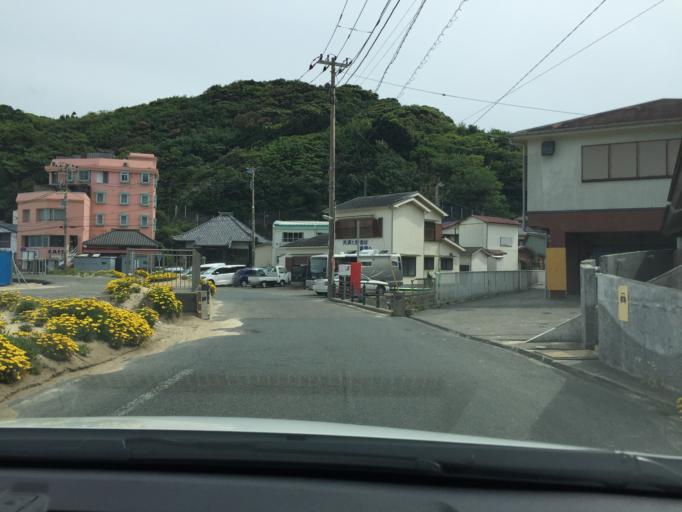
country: JP
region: Shizuoka
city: Shimoda
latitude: 34.6736
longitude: 138.9723
